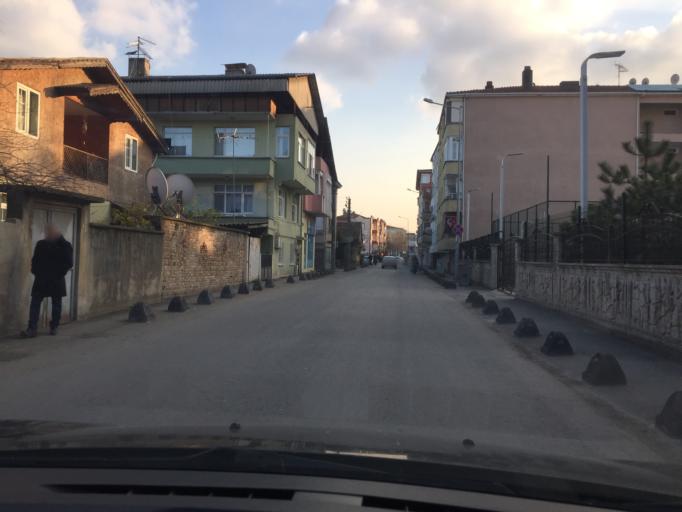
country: TR
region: Sakarya
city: Adapazari
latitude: 40.7831
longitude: 30.4018
